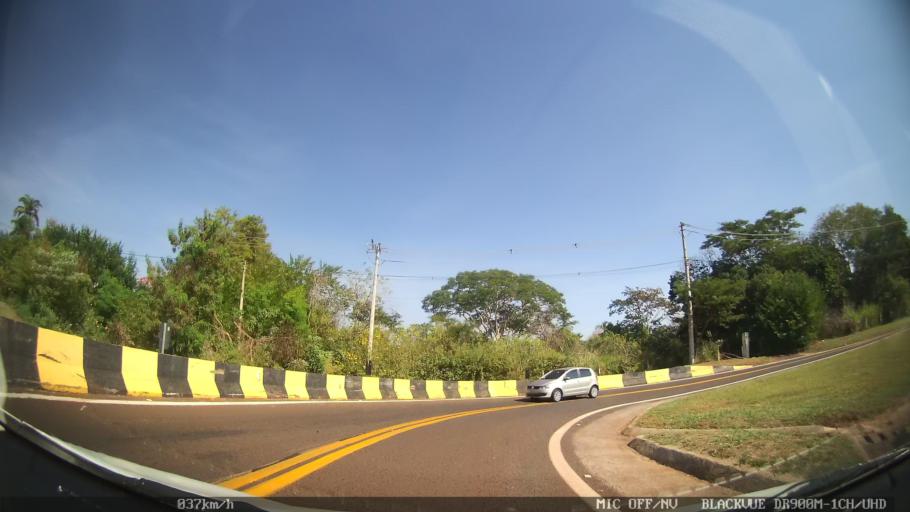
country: BR
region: Sao Paulo
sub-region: Ribeirao Preto
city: Ribeirao Preto
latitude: -21.2165
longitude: -47.8359
